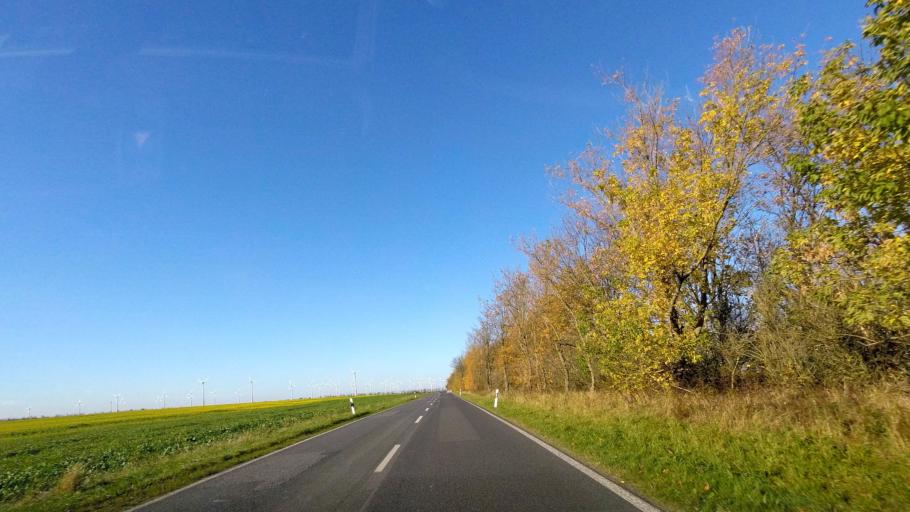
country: DE
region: Saxony-Anhalt
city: Zahna
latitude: 51.9776
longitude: 12.8606
